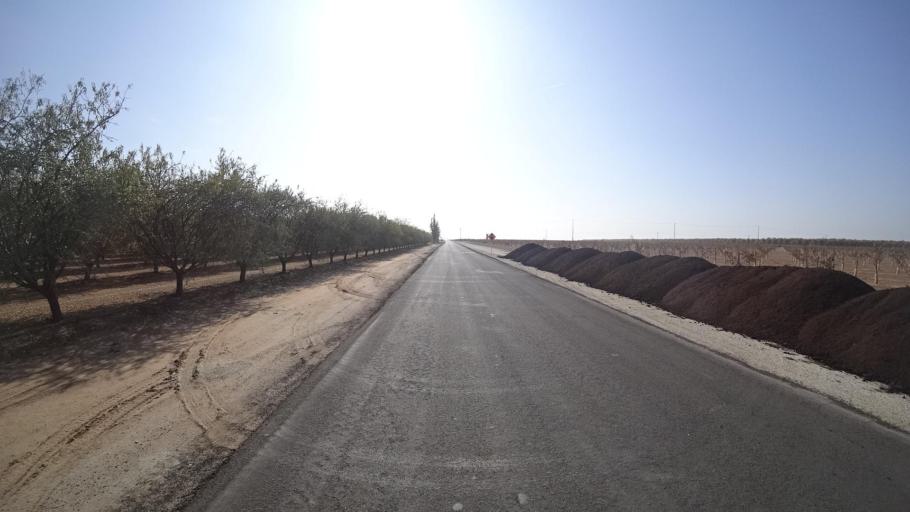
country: US
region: California
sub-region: Kern County
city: McFarland
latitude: 35.6336
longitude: -119.1867
